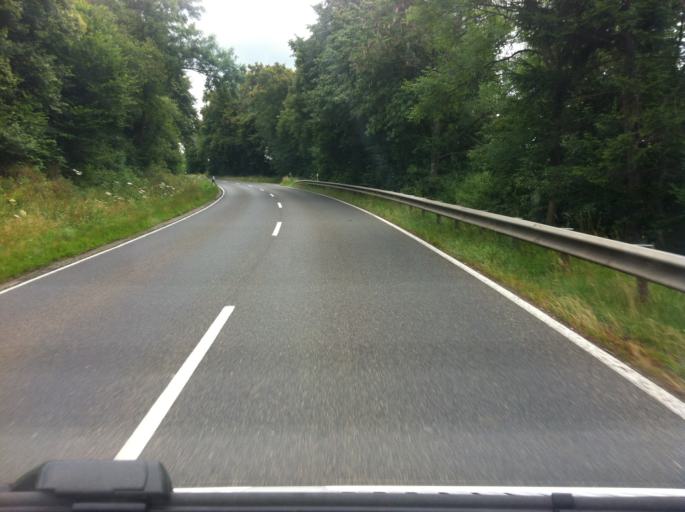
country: DE
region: North Rhine-Westphalia
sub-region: Regierungsbezirk Koln
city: Nettersheim
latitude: 50.5196
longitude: 6.6542
